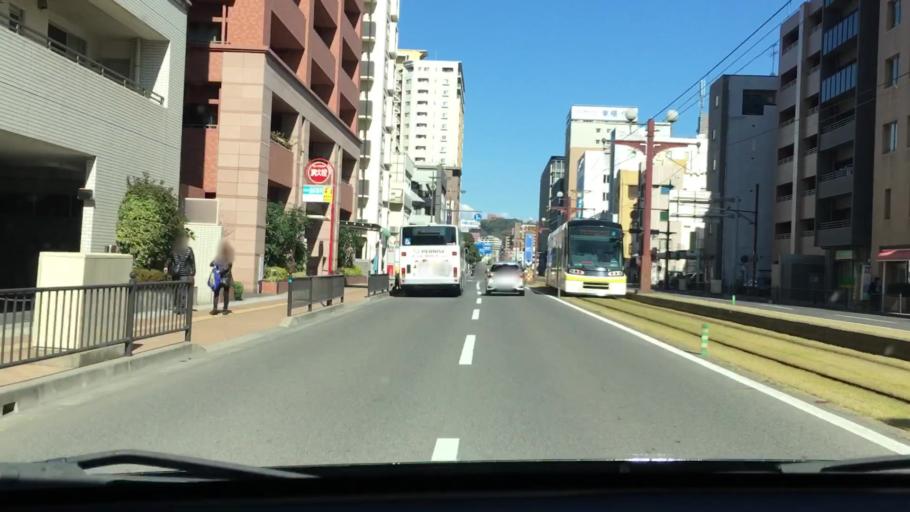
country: JP
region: Kagoshima
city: Kagoshima-shi
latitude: 31.5798
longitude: 130.5428
